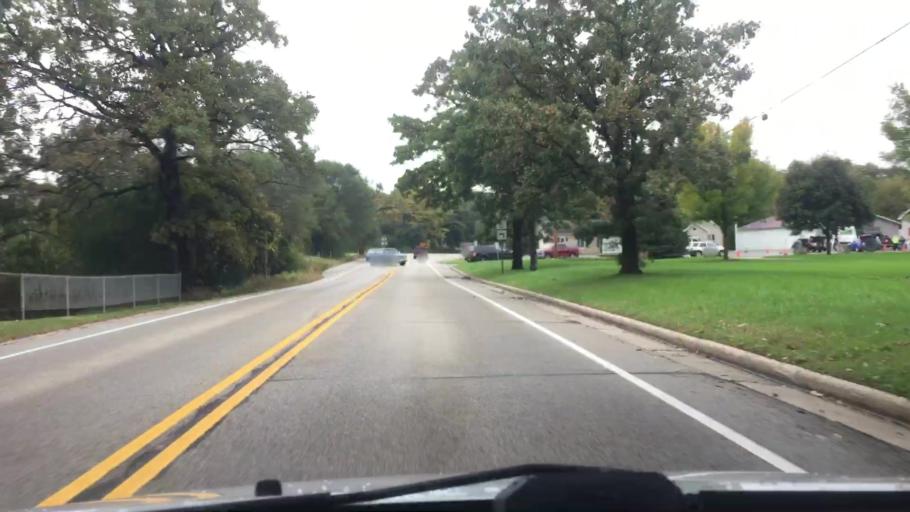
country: US
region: Wisconsin
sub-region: Waukesha County
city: Dousman
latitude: 42.9853
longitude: -88.4638
